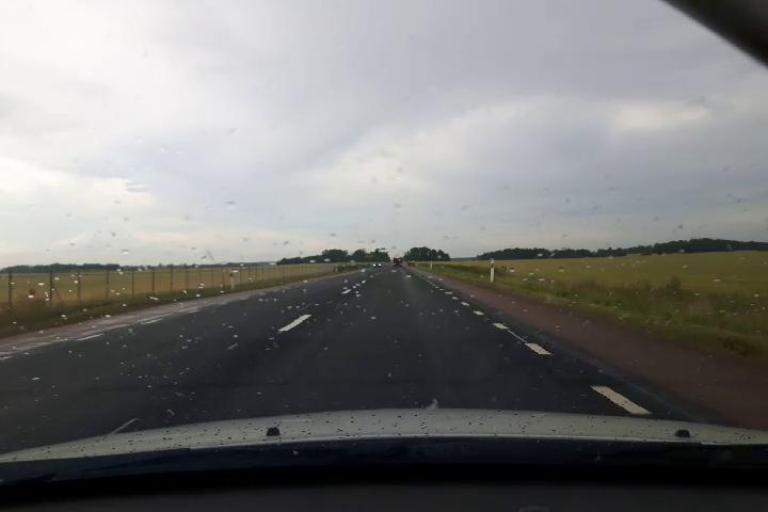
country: SE
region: Uppsala
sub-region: Uppsala Kommun
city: Gamla Uppsala
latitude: 59.9516
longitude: 17.5877
